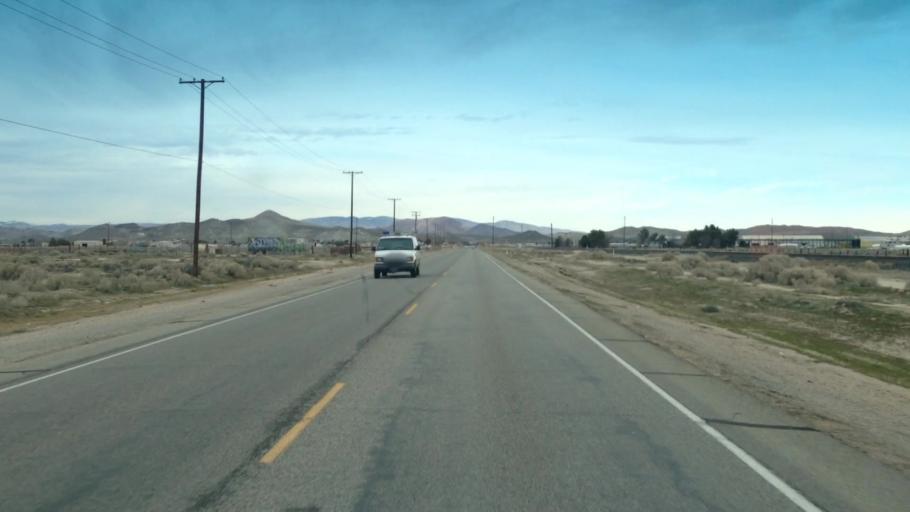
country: US
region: California
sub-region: Kern County
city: Rosamond
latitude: 34.8301
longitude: -118.1576
